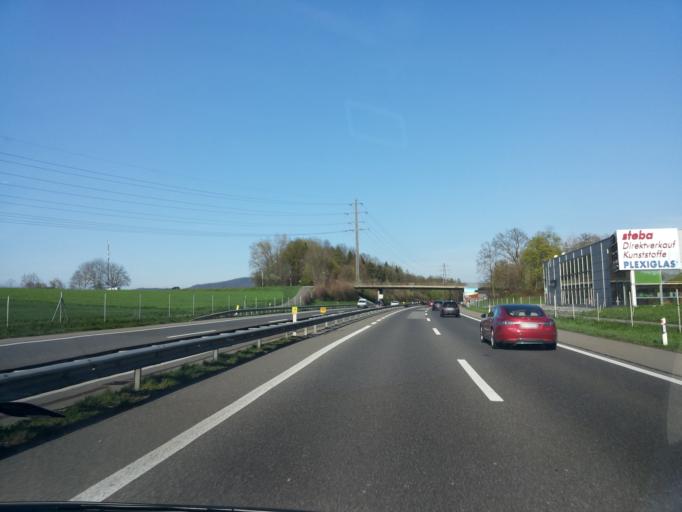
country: CH
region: Aargau
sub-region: Bezirk Brugg
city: Rupperswil
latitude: 47.3898
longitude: 8.1221
